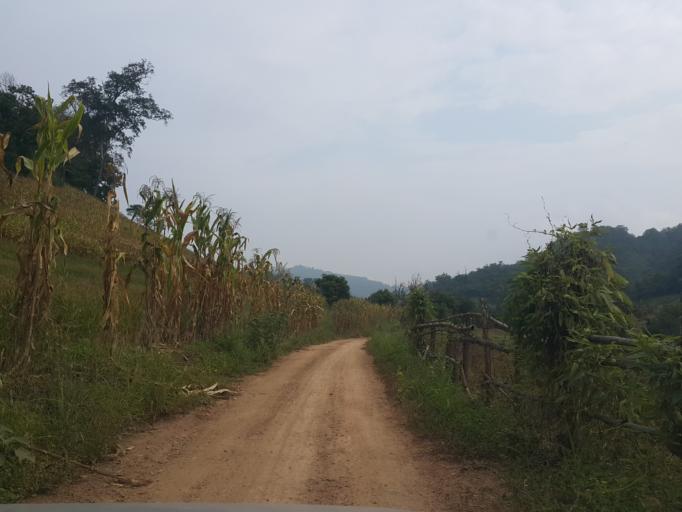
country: TH
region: Mae Hong Son
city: Wiang Nuea
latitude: 19.3905
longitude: 98.4683
